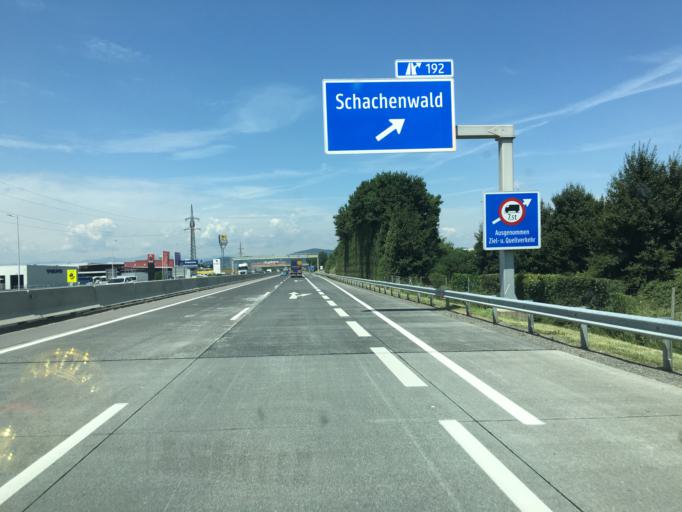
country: AT
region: Styria
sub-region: Politischer Bezirk Graz-Umgebung
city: Zettling
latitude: 46.9711
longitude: 15.4302
